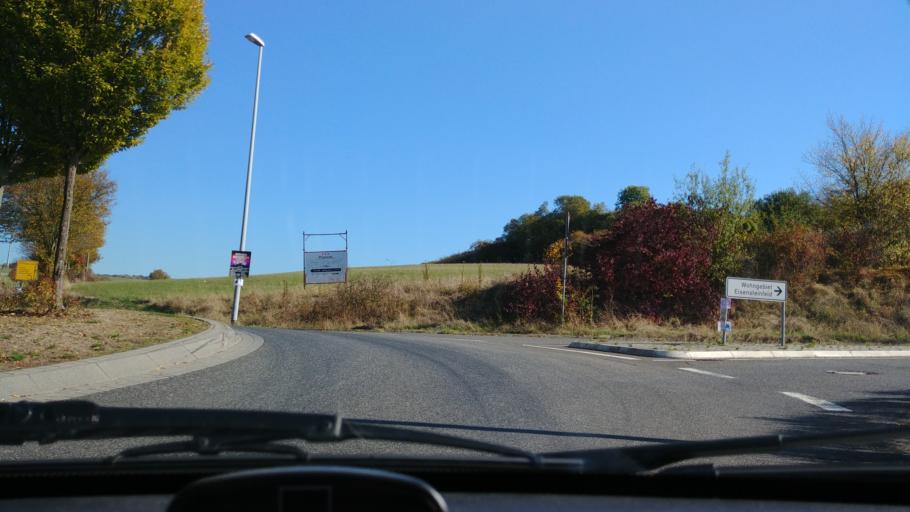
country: DE
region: Rheinland-Pfalz
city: Katzenelnbogen
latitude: 50.2692
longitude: 7.9832
